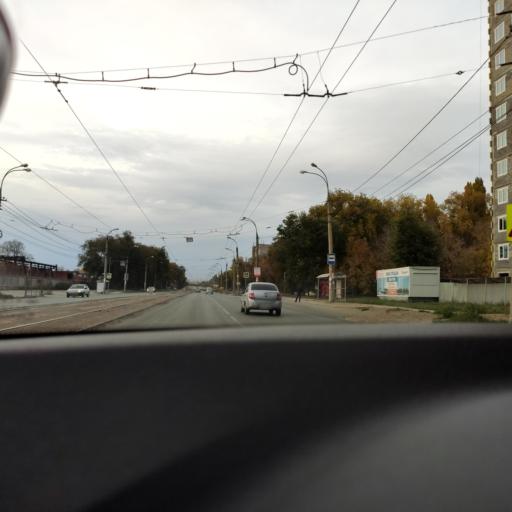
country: RU
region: Samara
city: Smyshlyayevka
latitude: 53.2018
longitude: 50.2837
